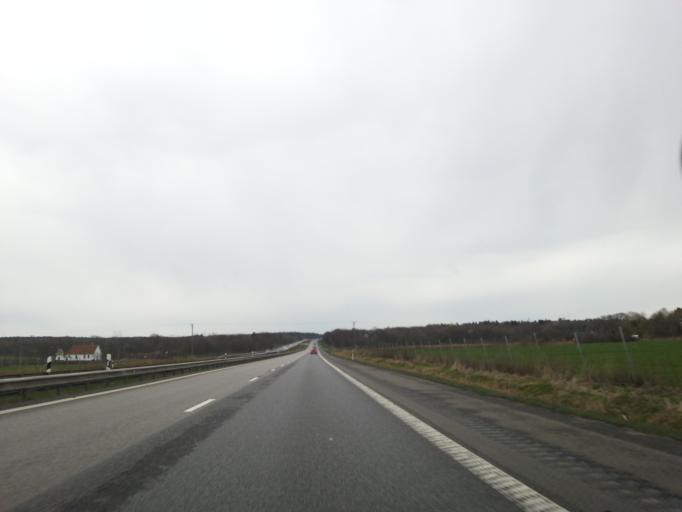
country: SE
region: Halland
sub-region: Kungsbacka Kommun
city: Frillesas
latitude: 57.3024
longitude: 12.2146
